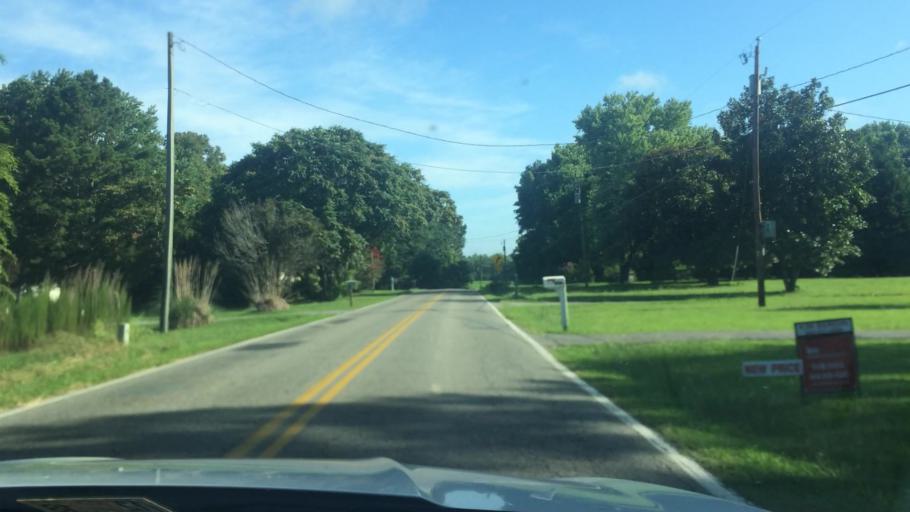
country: US
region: Virginia
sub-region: Middlesex County
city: Deltaville
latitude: 37.5797
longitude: -76.4567
